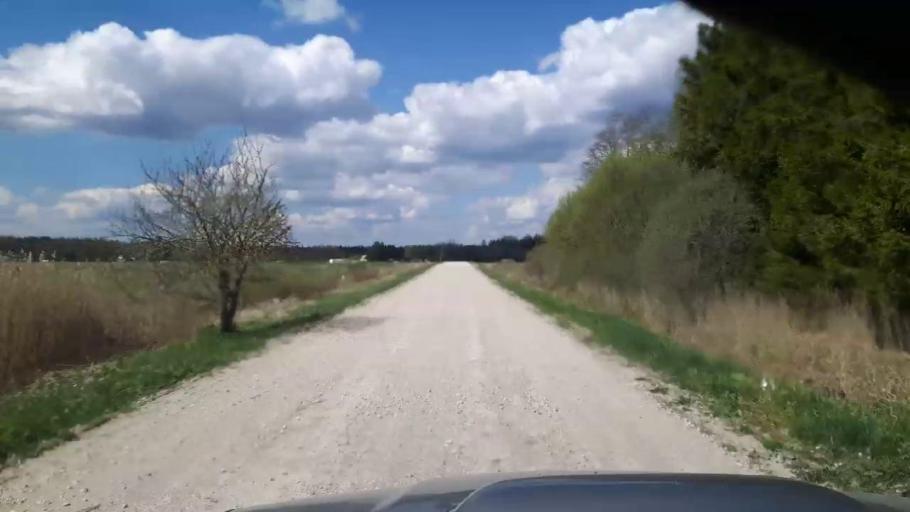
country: EE
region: Paernumaa
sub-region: Tootsi vald
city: Tootsi
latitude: 58.4614
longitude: 24.8730
